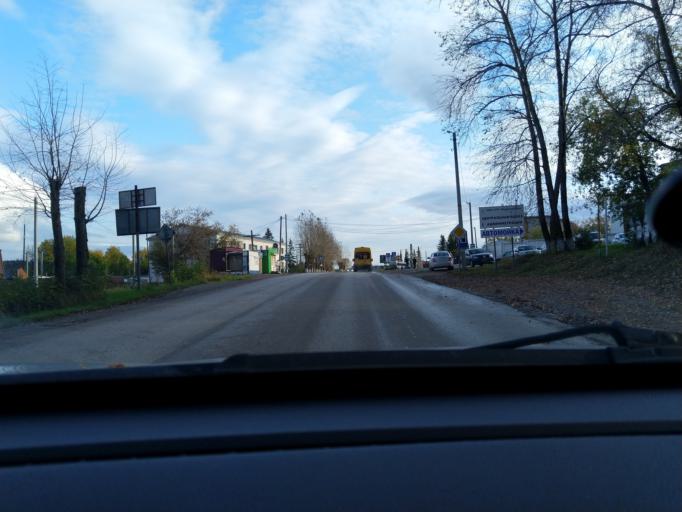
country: RU
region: Perm
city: Polazna
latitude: 58.2850
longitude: 56.4104
